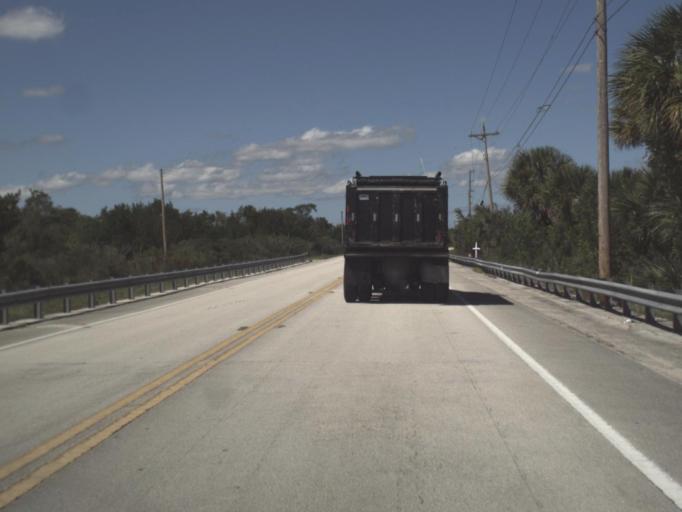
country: US
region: Florida
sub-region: Collier County
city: Marco
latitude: 25.9729
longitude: -81.5506
